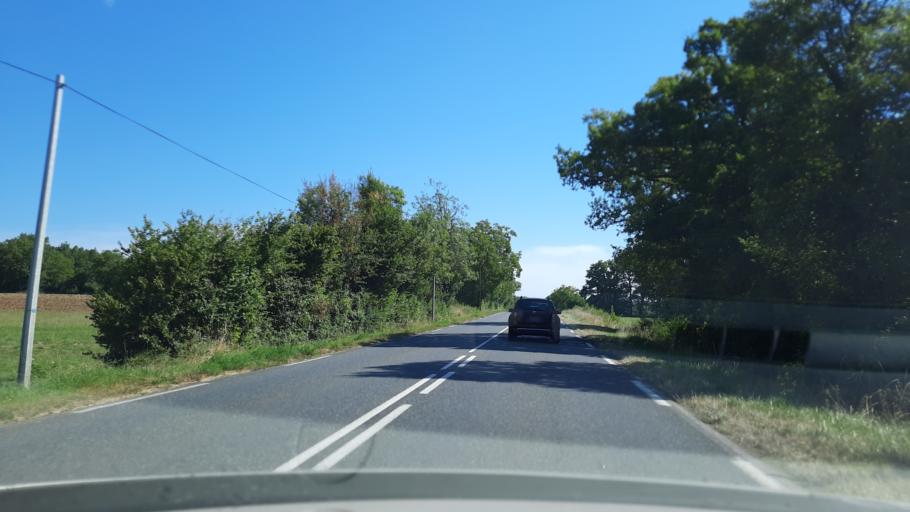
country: FR
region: Midi-Pyrenees
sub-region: Departement du Tarn-et-Garonne
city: Caylus
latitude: 44.3081
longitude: 1.8832
